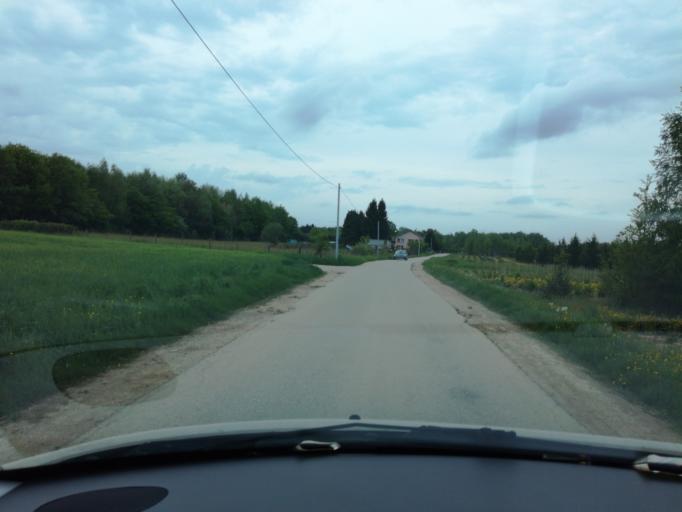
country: FR
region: Rhone-Alpes
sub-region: Departement de l'Ain
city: Certines
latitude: 46.1540
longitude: 5.2636
